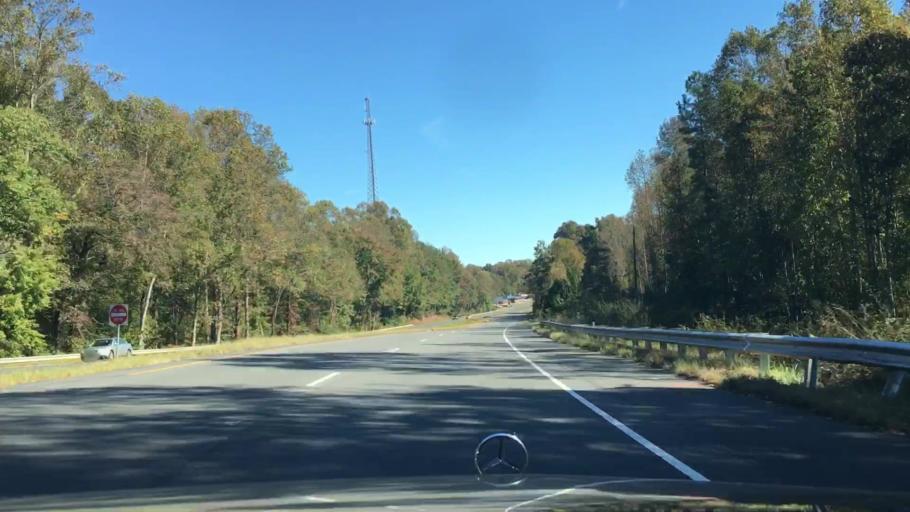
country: US
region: Virginia
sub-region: King George County
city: King George
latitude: 38.2783
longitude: -77.2290
